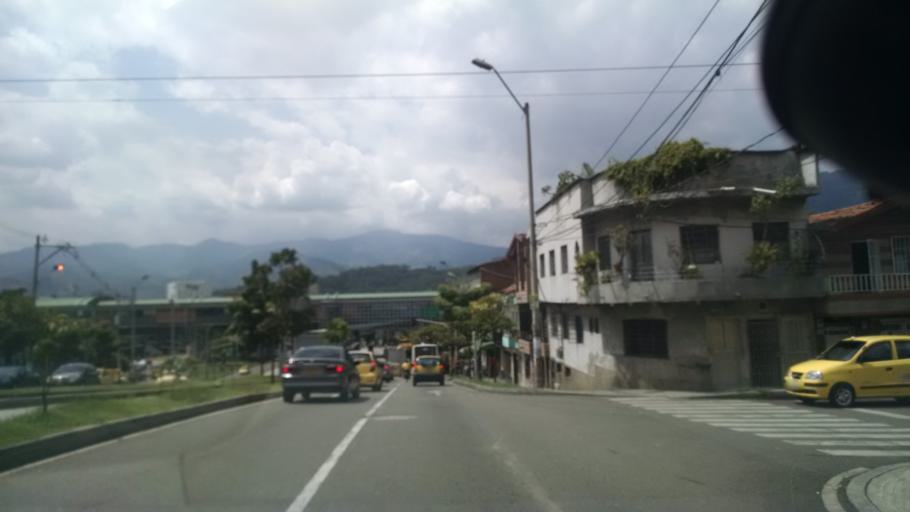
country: CO
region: Antioquia
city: Medellin
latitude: 6.2639
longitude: -75.5617
